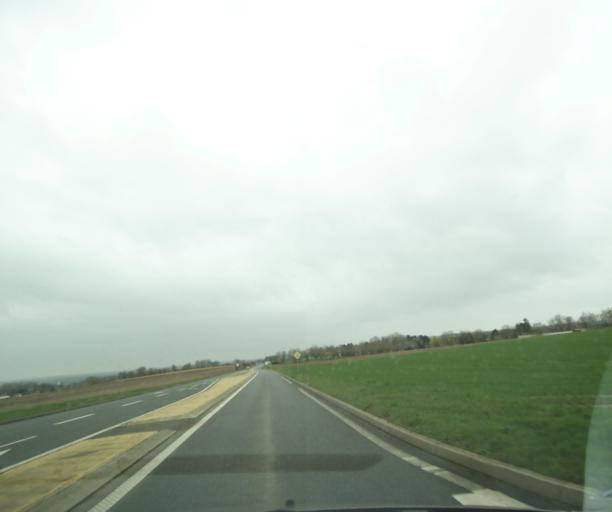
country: FR
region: Picardie
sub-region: Departement de l'Oise
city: Noyon
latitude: 49.6013
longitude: 3.0114
